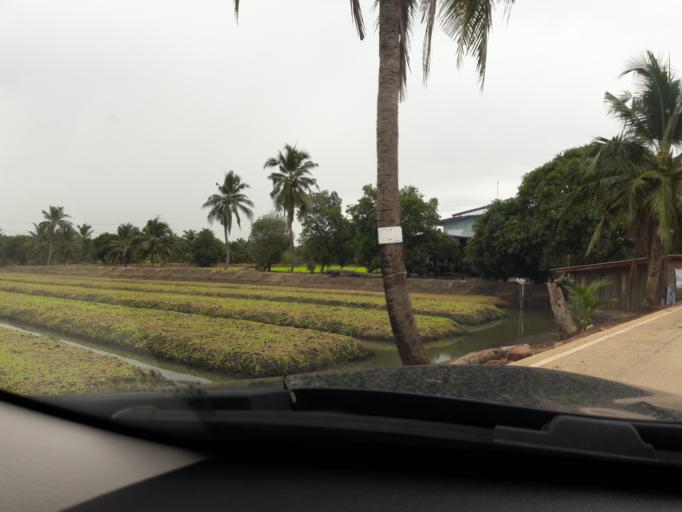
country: TH
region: Ratchaburi
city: Bang Phae
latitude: 13.6088
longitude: 99.9663
